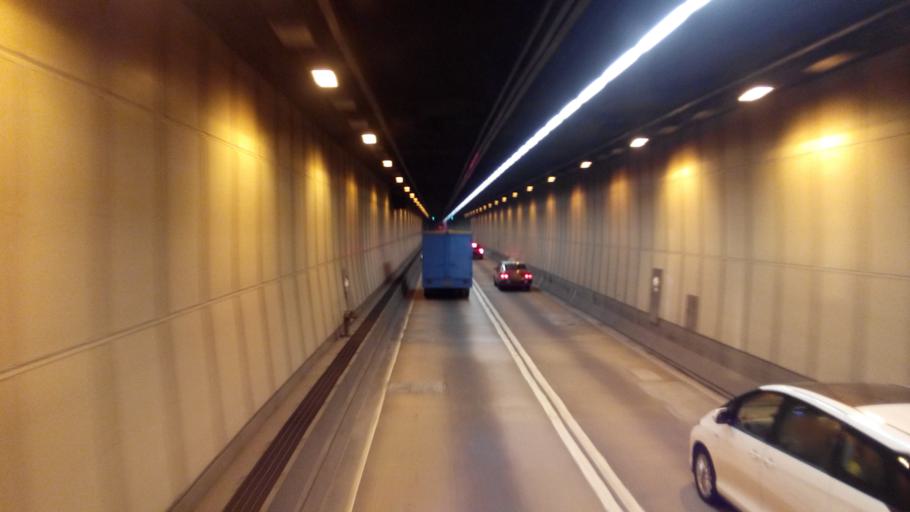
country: HK
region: Wanchai
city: Wan Chai
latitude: 22.2696
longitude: 114.1810
